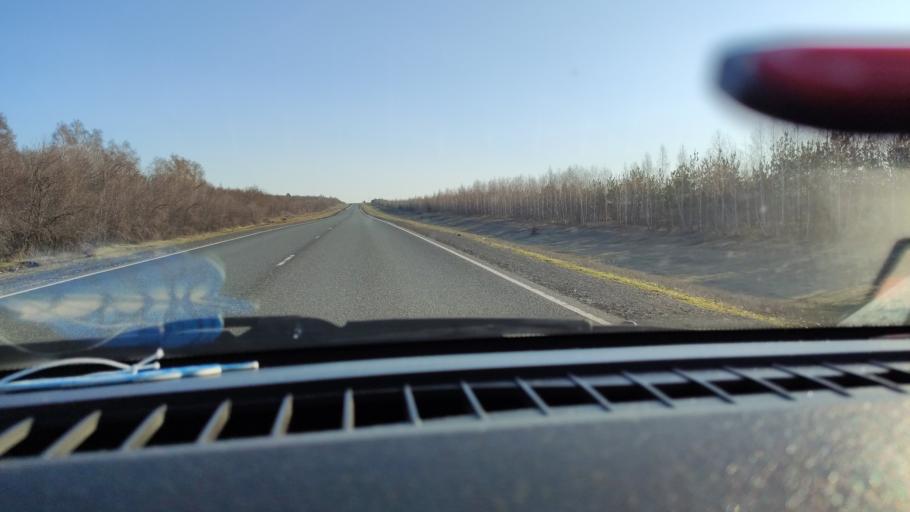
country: RU
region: Saratov
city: Balakovo
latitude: 52.1511
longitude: 47.8112
